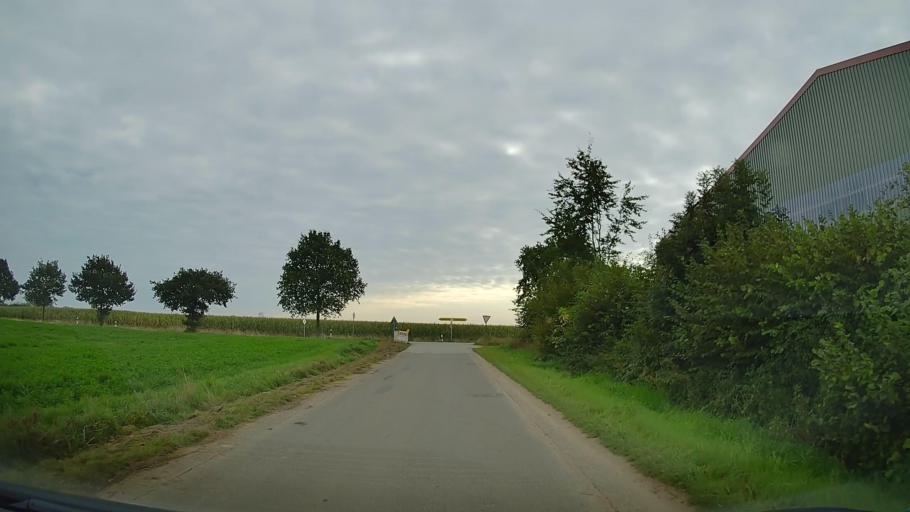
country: DE
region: Schleswig-Holstein
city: Hohenfelde
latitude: 54.3672
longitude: 10.5417
